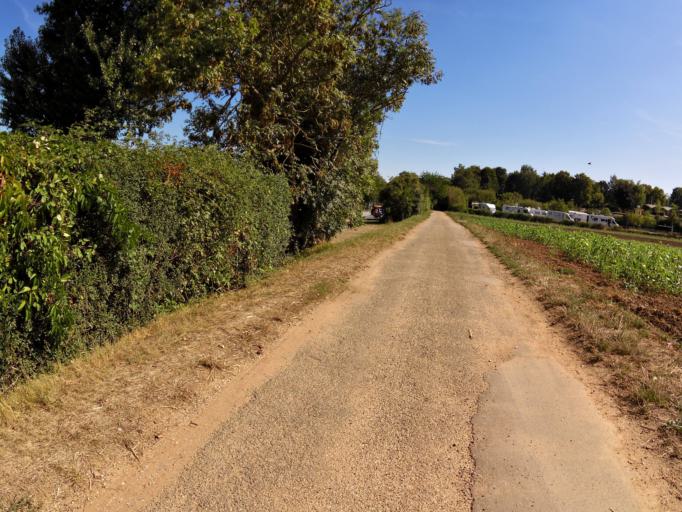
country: DE
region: Baden-Wuerttemberg
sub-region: Regierungsbezirk Stuttgart
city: Lauffen am Neckar
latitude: 49.0705
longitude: 9.1625
